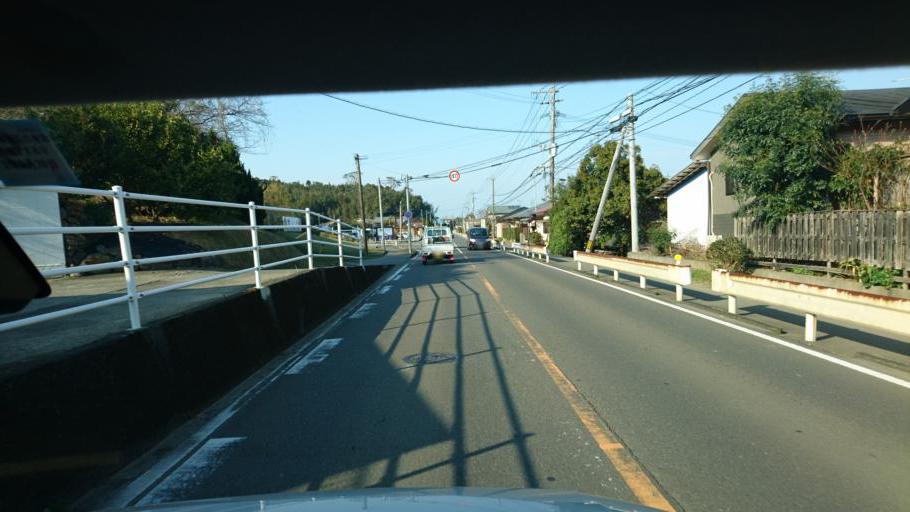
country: JP
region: Miyazaki
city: Miyazaki-shi
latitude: 31.9803
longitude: 131.4400
